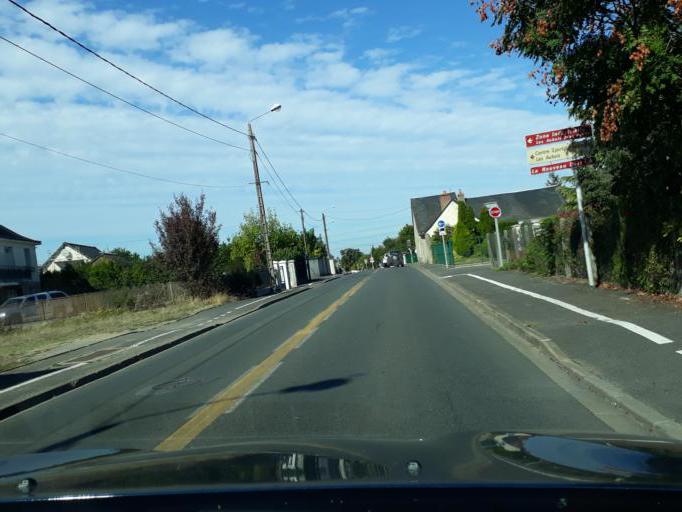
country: FR
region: Centre
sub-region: Departement d'Indre-et-Loire
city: Saint-Avertin
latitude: 47.3458
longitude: 0.7352
